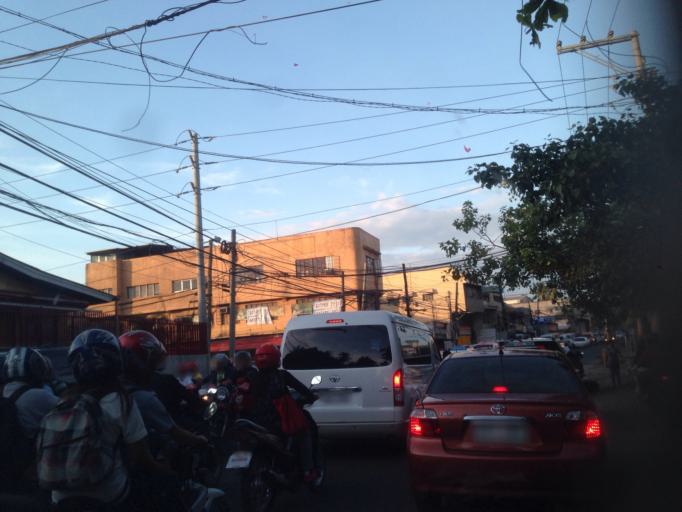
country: PH
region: Central Visayas
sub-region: Cebu City
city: Baugo
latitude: 10.3116
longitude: 123.9096
